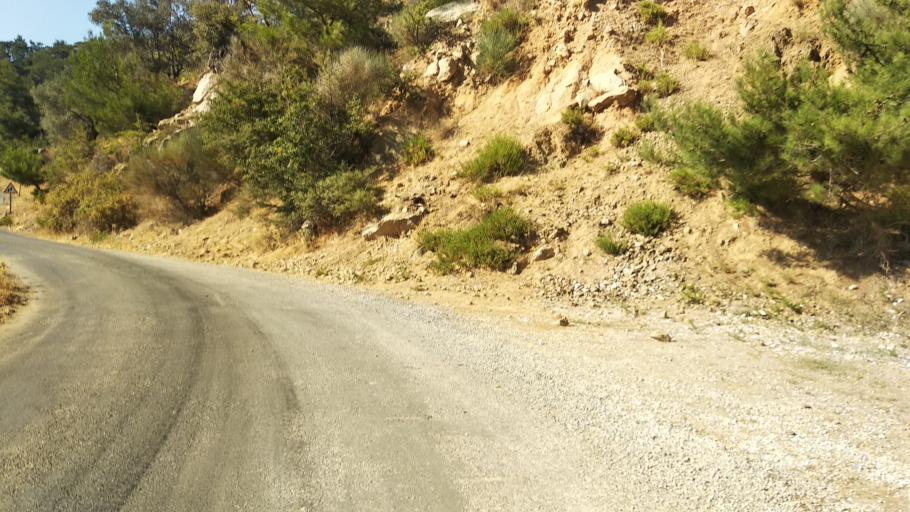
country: TR
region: Izmir
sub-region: Seferihisar
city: Seferhisar
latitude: 38.3191
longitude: 26.9582
